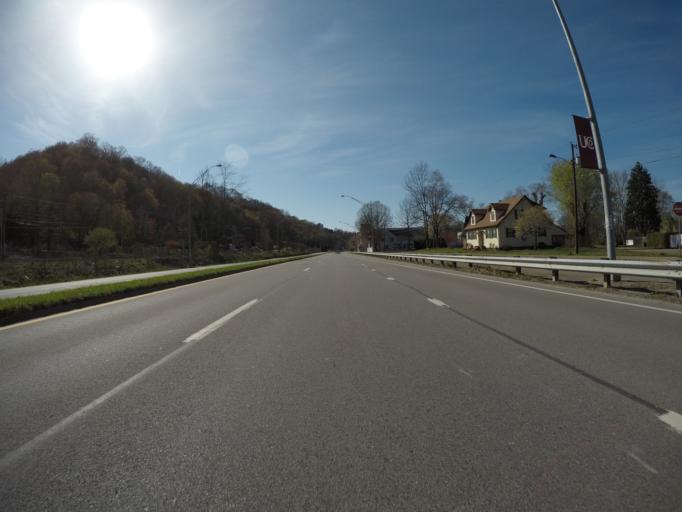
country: US
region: West Virginia
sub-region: Kanawha County
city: Charleston
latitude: 38.3307
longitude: -81.6125
